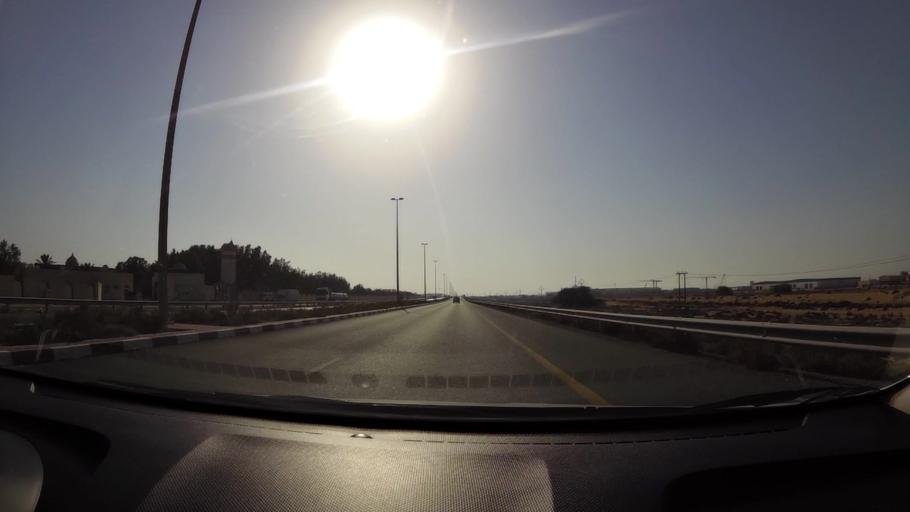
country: AE
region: Umm al Qaywayn
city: Umm al Qaywayn
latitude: 25.4325
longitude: 55.5747
